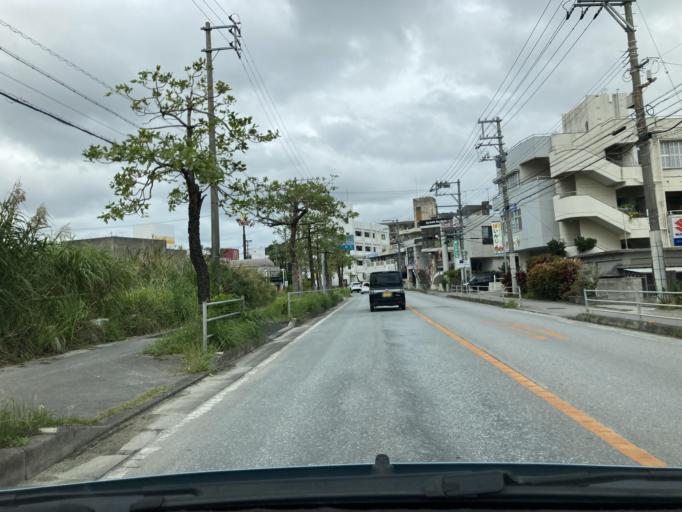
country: JP
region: Okinawa
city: Ginowan
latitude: 26.2376
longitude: 127.7497
